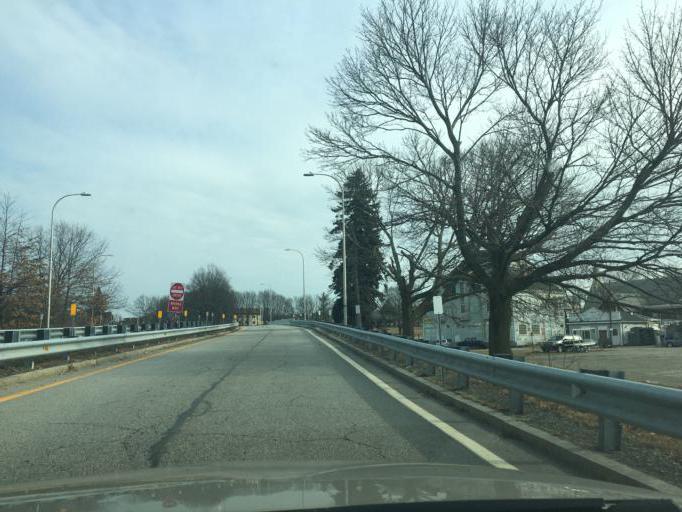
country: US
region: Rhode Island
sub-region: Providence County
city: East Providence
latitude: 41.8170
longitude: -71.3831
